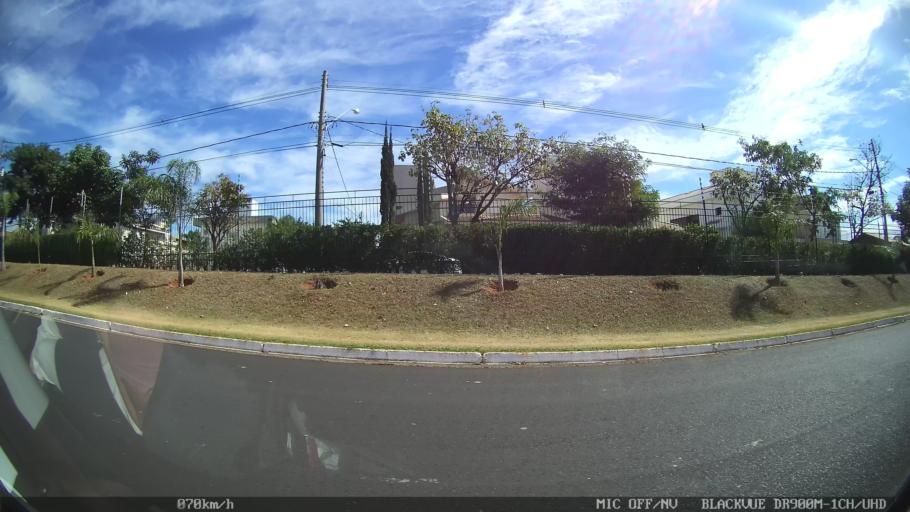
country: BR
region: Sao Paulo
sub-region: Sao Jose Do Rio Preto
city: Sao Jose do Rio Preto
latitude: -20.8204
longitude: -49.4813
